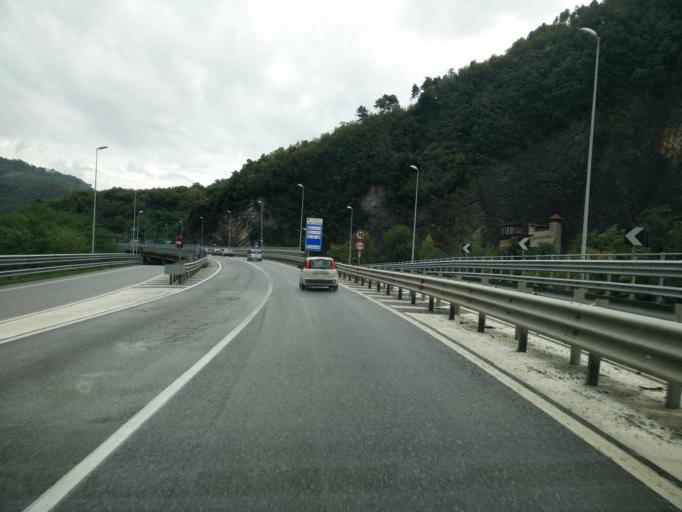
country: IT
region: Tuscany
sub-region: Provincia di Lucca
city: Valdottavo
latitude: 43.9267
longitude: 10.5175
